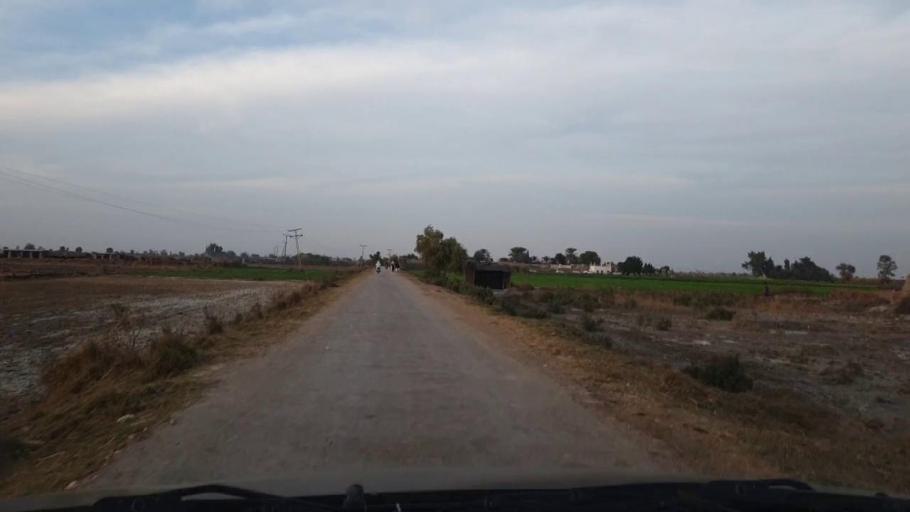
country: PK
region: Sindh
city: Khadro
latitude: 26.1347
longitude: 68.7570
